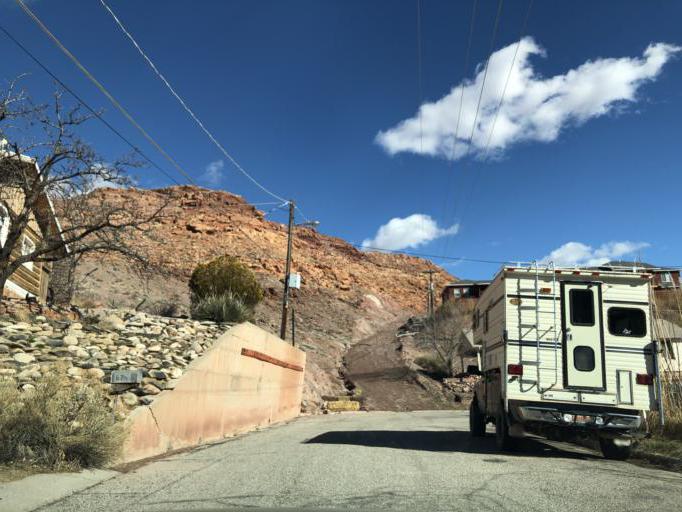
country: US
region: Utah
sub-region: Grand County
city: Moab
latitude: 38.5722
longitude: -109.5385
